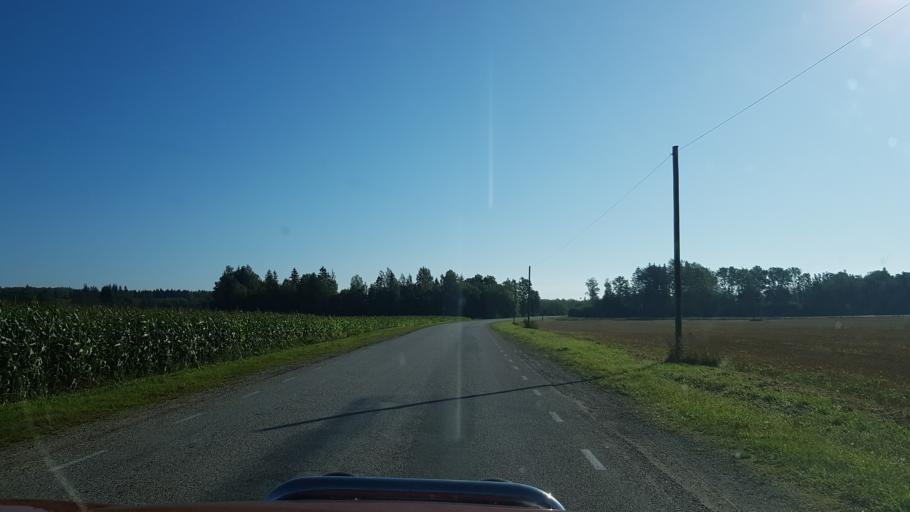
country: EE
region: Jogevamaa
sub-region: Tabivere vald
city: Tabivere
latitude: 58.6842
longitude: 26.5961
